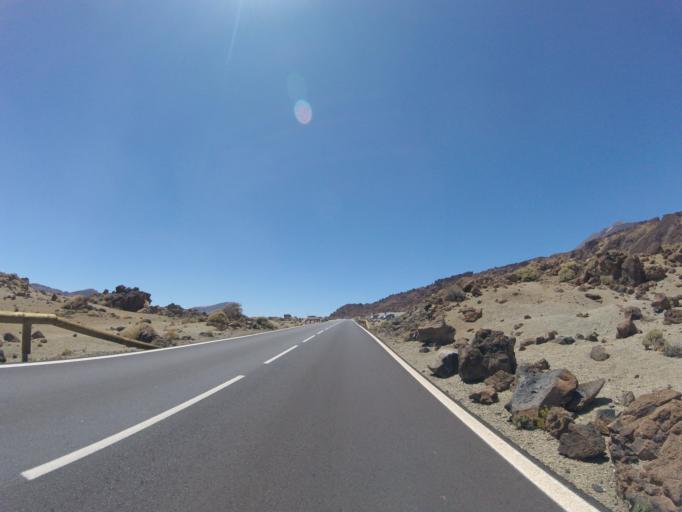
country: ES
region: Canary Islands
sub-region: Provincia de Santa Cruz de Tenerife
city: Los Realejos
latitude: 28.2665
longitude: -16.5876
